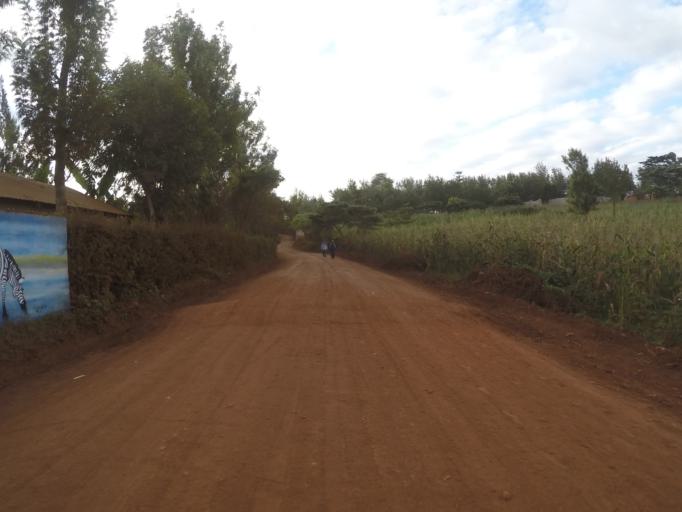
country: TZ
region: Arusha
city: Kiratu
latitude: -3.3285
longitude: 35.6659
